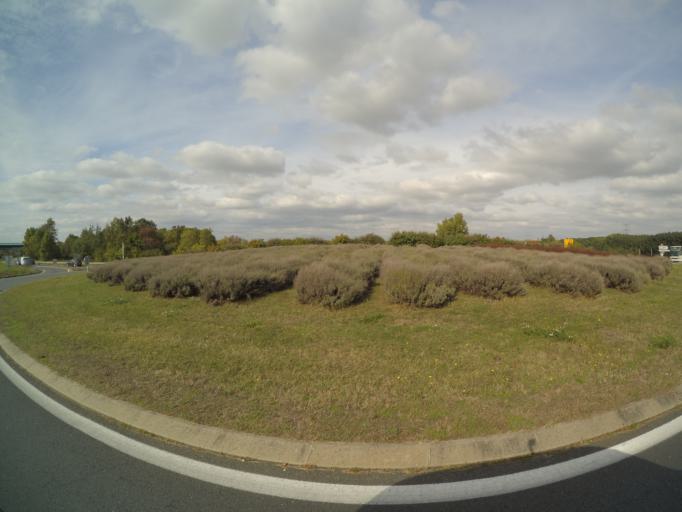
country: FR
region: Centre
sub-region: Departement d'Indre-et-Loire
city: Vouvray
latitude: 47.4037
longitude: 0.8068
